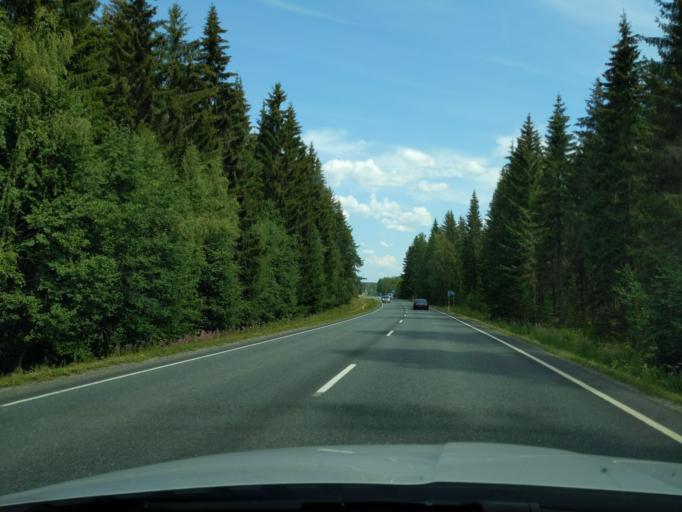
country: FI
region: Haeme
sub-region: Haemeenlinna
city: Tuulos
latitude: 61.0999
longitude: 24.8424
